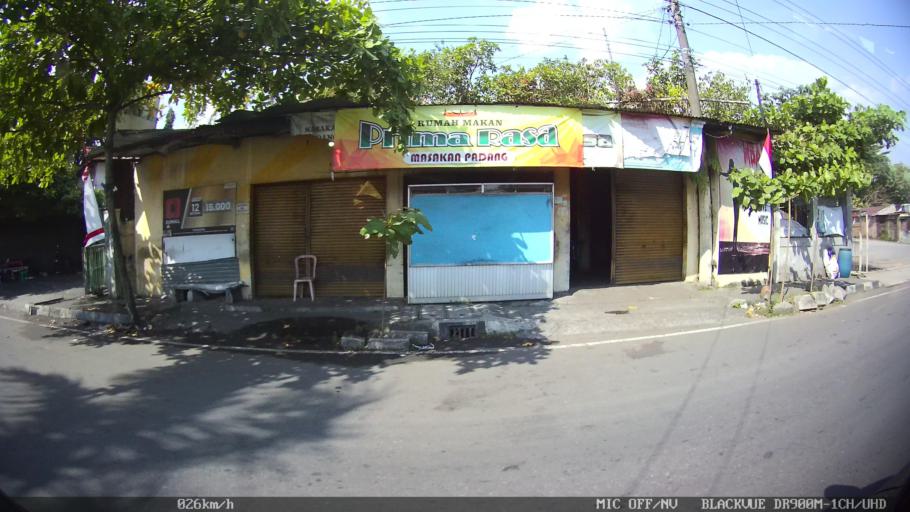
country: ID
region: Daerah Istimewa Yogyakarta
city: Sewon
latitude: -7.8349
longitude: 110.3911
